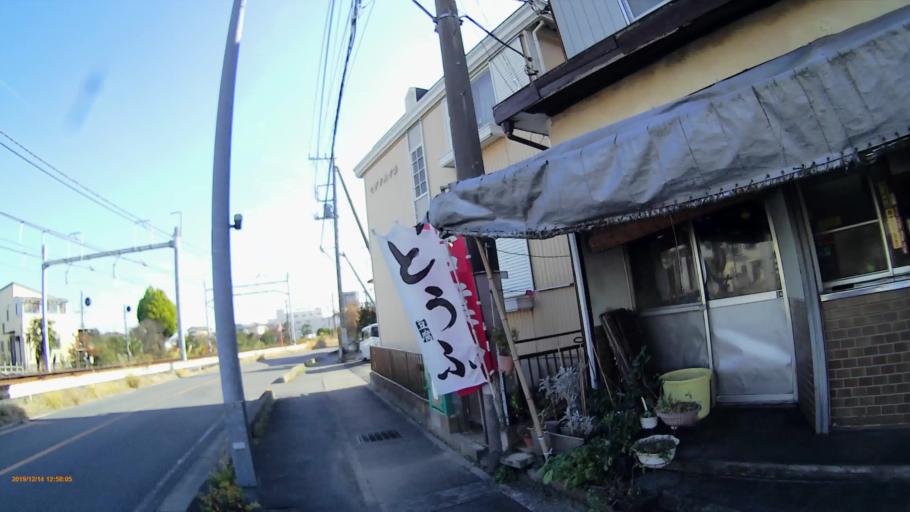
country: JP
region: Saitama
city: Fukiage-fujimi
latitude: 36.1001
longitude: 139.4597
